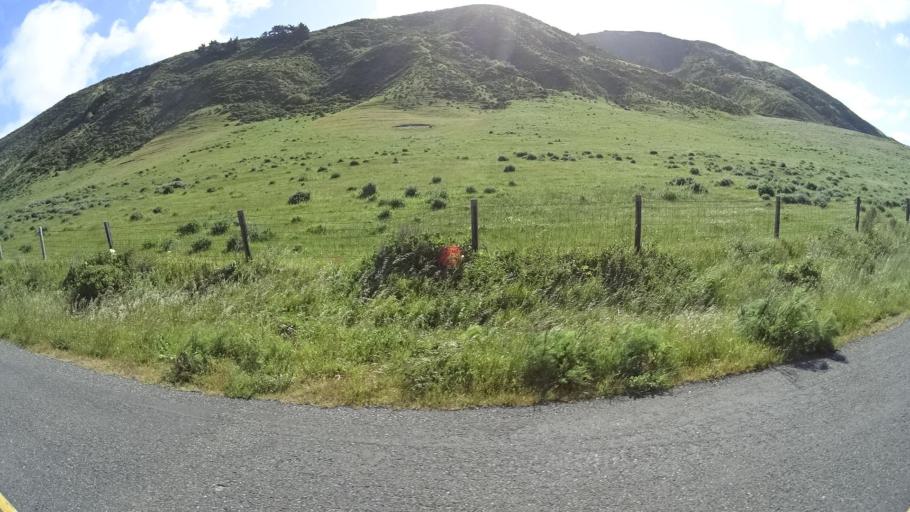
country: US
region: California
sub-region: Humboldt County
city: Ferndale
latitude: 40.4215
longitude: -124.3990
